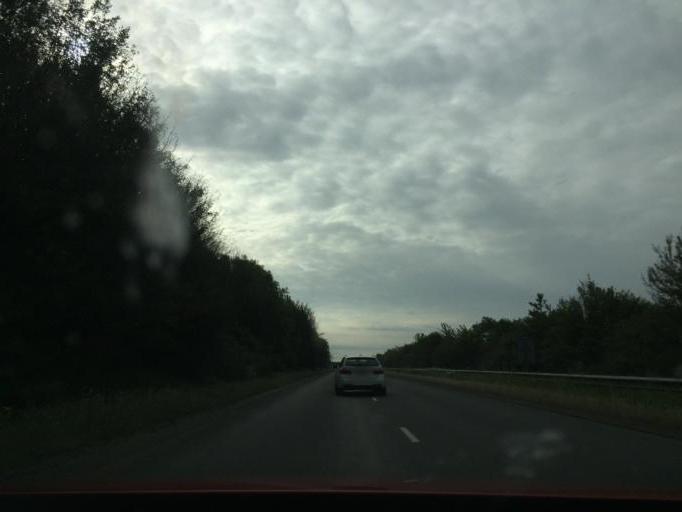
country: GB
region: England
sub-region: Leicestershire
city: Lutterworth
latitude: 52.4522
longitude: -1.2203
